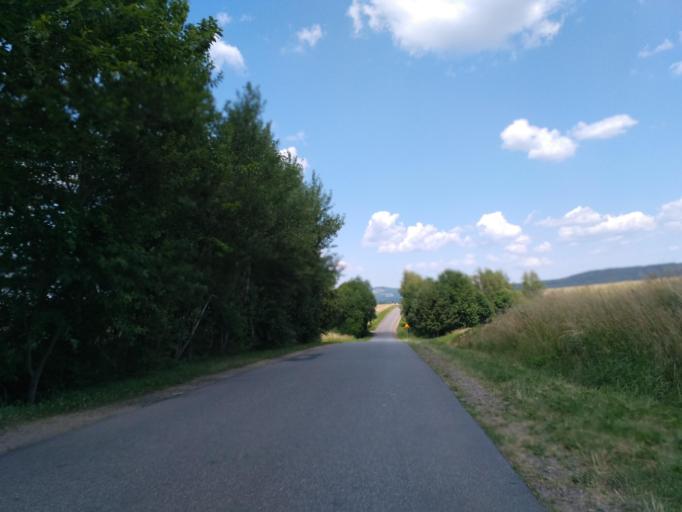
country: PL
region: Subcarpathian Voivodeship
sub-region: Powiat sanocki
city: Strachocina
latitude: 49.5848
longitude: 22.1280
